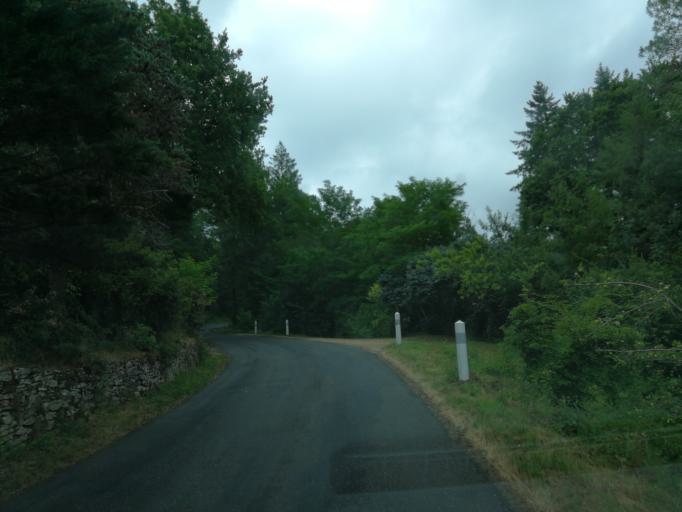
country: FR
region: Midi-Pyrenees
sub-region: Departement du Lot
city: Prayssac
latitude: 44.5375
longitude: 1.0860
